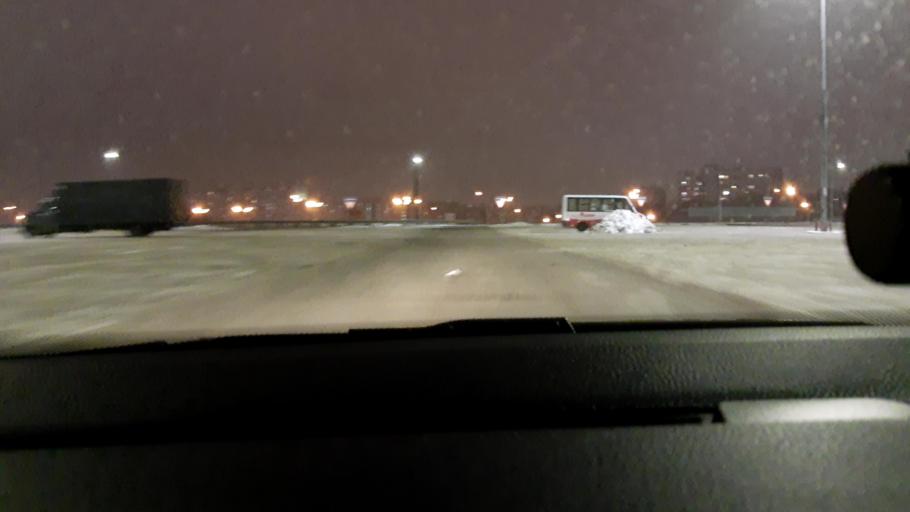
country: RU
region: Moscow
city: Vatutino
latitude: 55.8971
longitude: 37.6694
